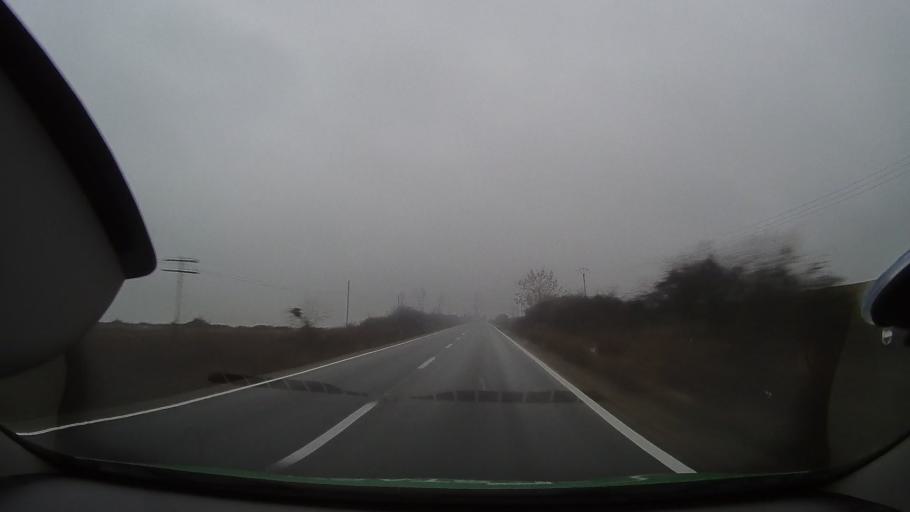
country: RO
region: Bihor
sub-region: Comuna Olcea
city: Calacea
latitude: 46.7187
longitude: 21.9520
